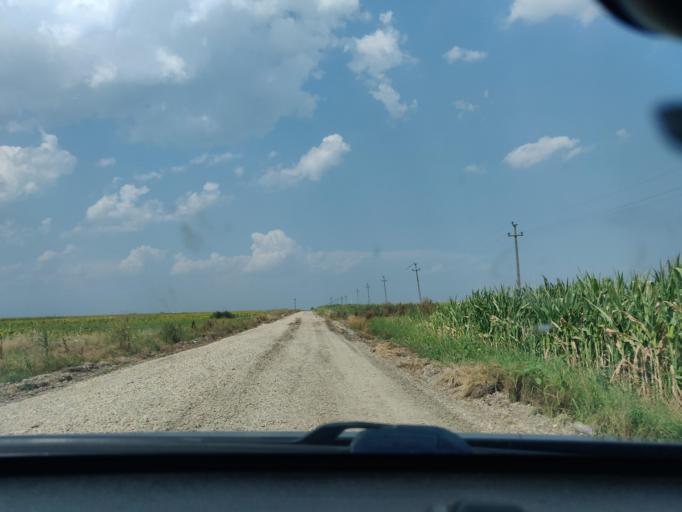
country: RO
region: Teleorman
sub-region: Comuna Sarbeni
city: Sarbeni
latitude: 44.4918
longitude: 25.3934
